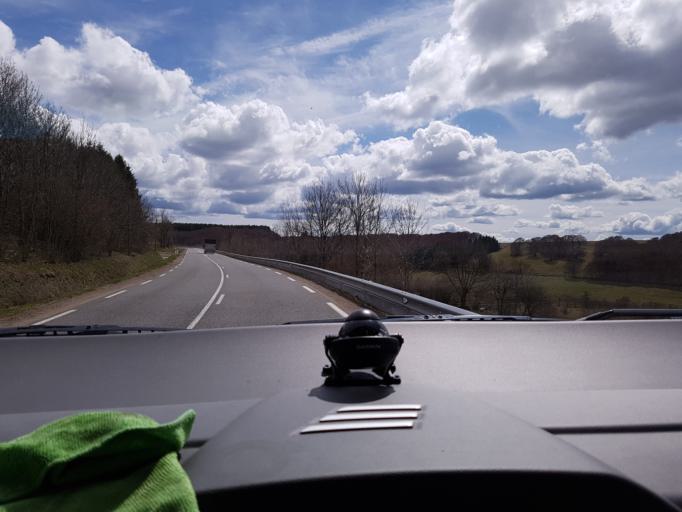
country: FR
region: Midi-Pyrenees
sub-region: Departement de l'Aveyron
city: Laguiole
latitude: 44.7482
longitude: 2.8703
